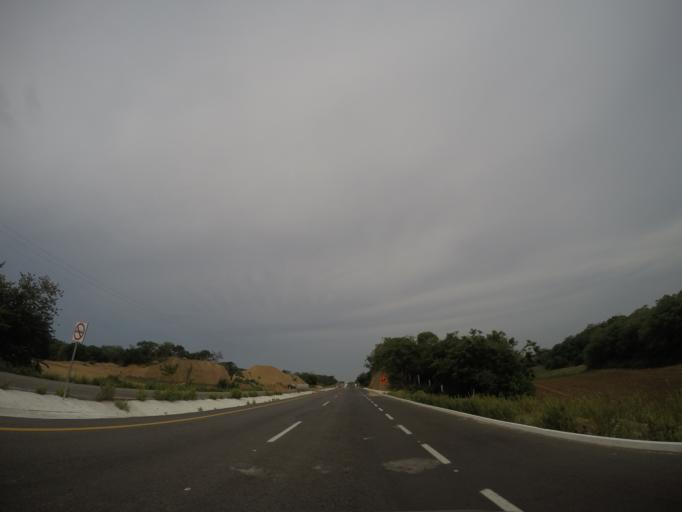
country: MX
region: Oaxaca
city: Santa Maria Tonameca
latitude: 15.7237
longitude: -96.6231
